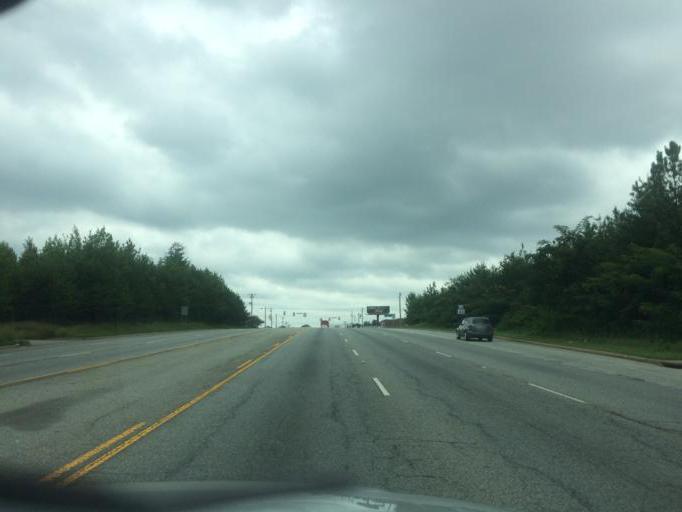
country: US
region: South Carolina
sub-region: Greenville County
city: Greer
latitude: 34.8913
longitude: -82.2329
